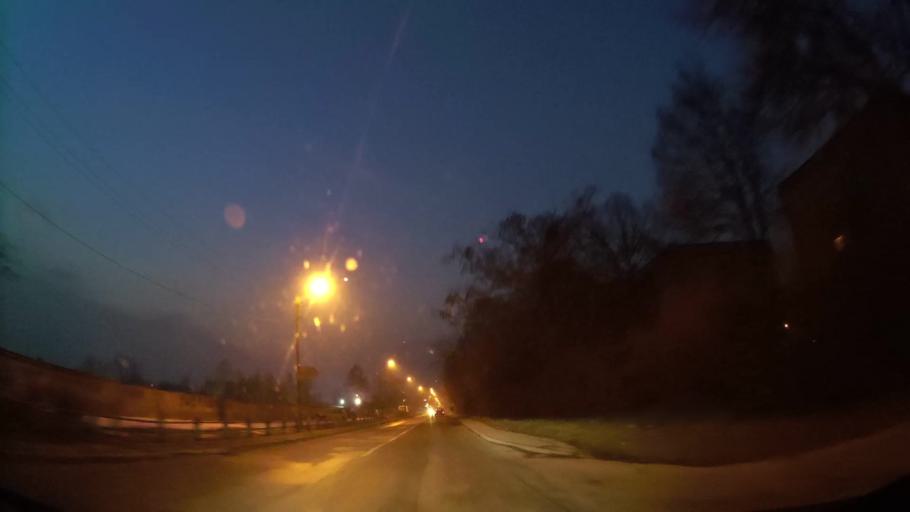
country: MK
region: Kisela Voda
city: Kisela Voda
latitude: 41.9983
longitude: 21.4925
